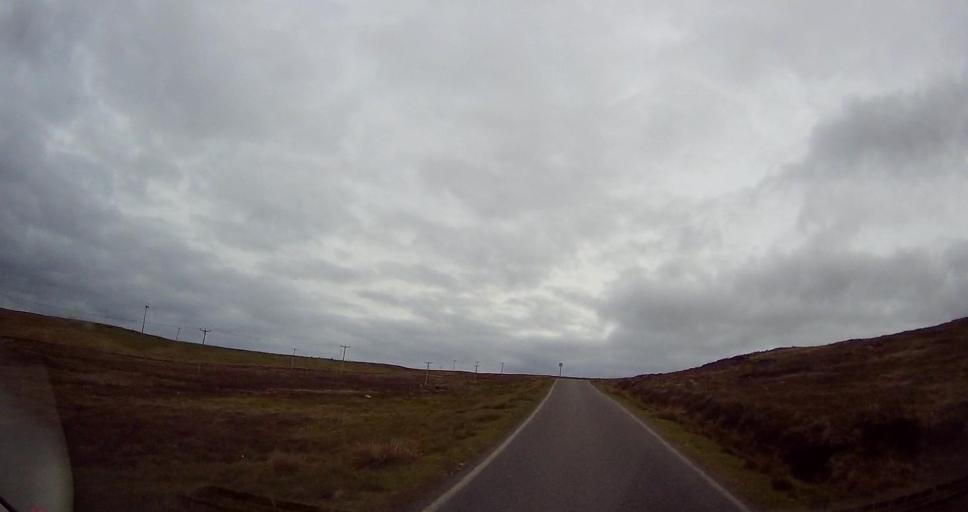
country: GB
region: Scotland
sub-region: Shetland Islands
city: Shetland
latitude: 60.5480
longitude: -1.0609
